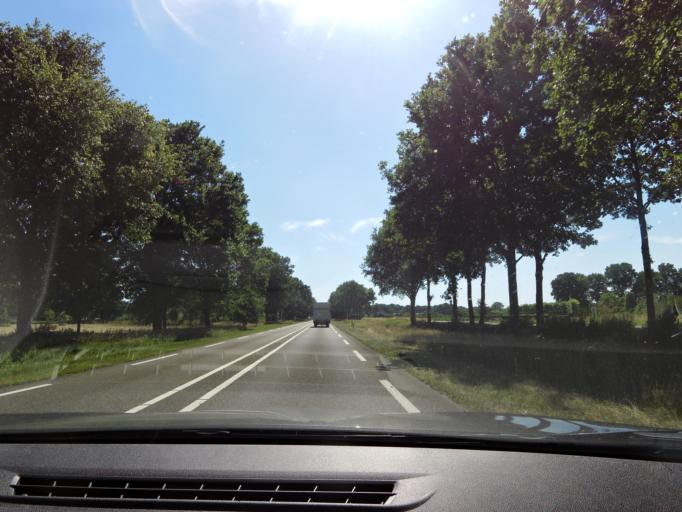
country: NL
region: Gelderland
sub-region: Oost Gelre
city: Lichtenvoorde
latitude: 51.9851
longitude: 6.5482
